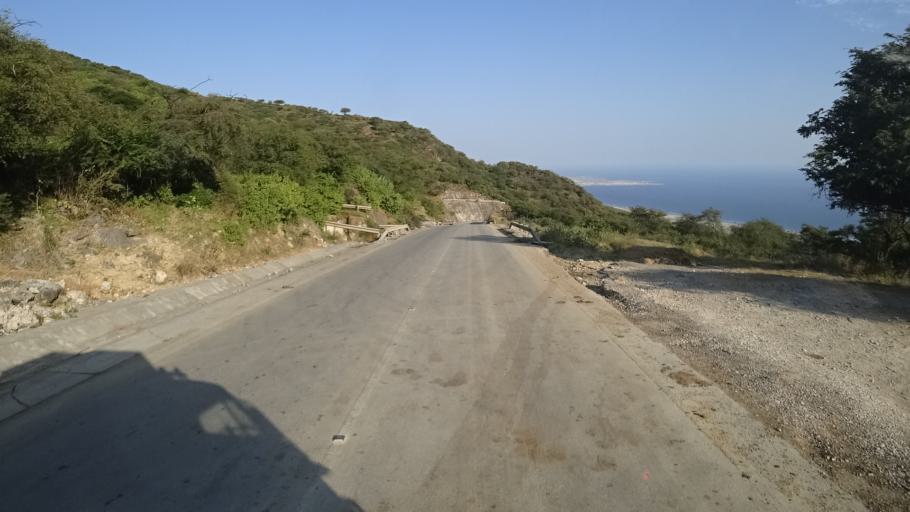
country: OM
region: Zufar
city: Salalah
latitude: 17.0604
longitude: 54.6105
